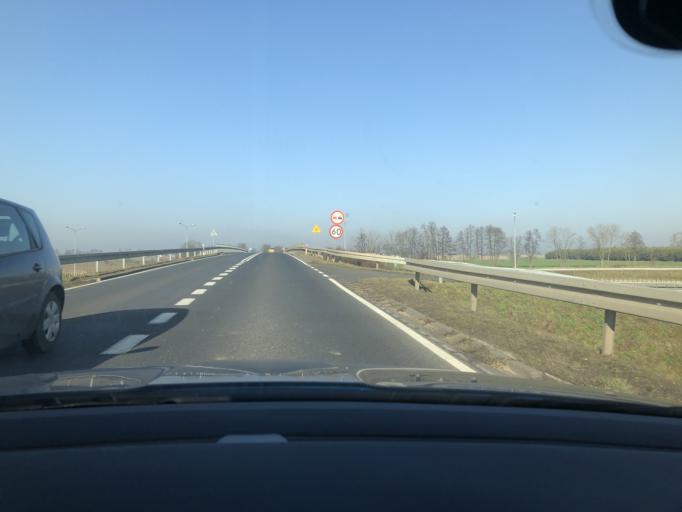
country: PL
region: Greater Poland Voivodeship
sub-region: Powiat poznanski
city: Buk
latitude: 52.3858
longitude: 16.4814
